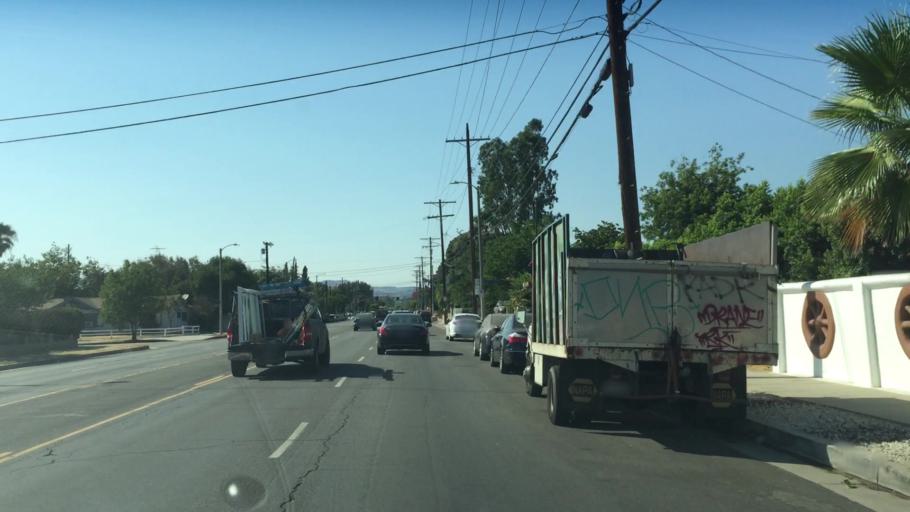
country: US
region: California
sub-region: Los Angeles County
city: San Fernando
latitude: 34.2518
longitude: -118.4363
